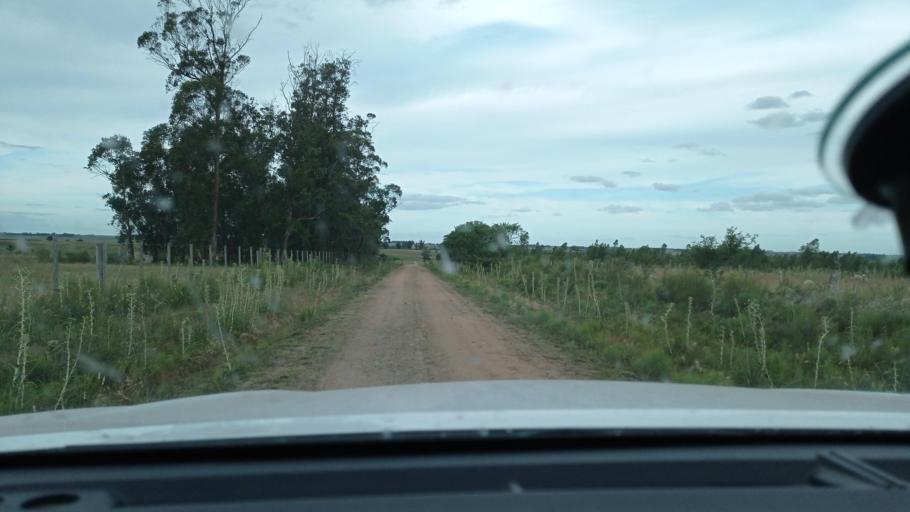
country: UY
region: Florida
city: Casupa
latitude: -34.1239
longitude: -55.8127
